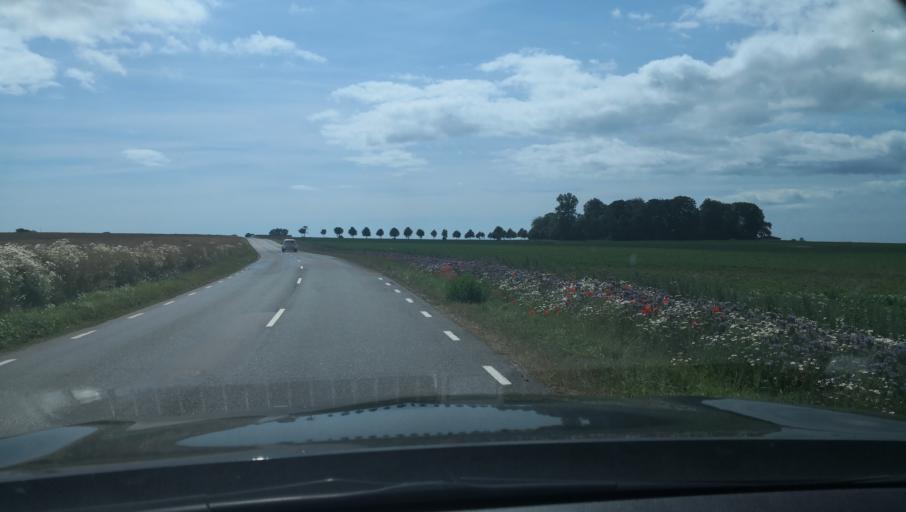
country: SE
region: Skane
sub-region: Tomelilla Kommun
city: Tomelilla
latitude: 55.4705
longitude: 14.0977
